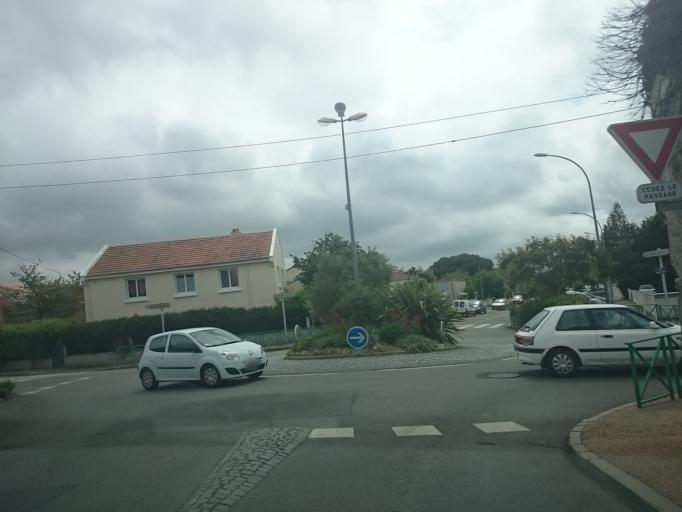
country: FR
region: Pays de la Loire
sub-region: Departement de la Loire-Atlantique
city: La Montagne
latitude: 47.1871
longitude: -1.6856
